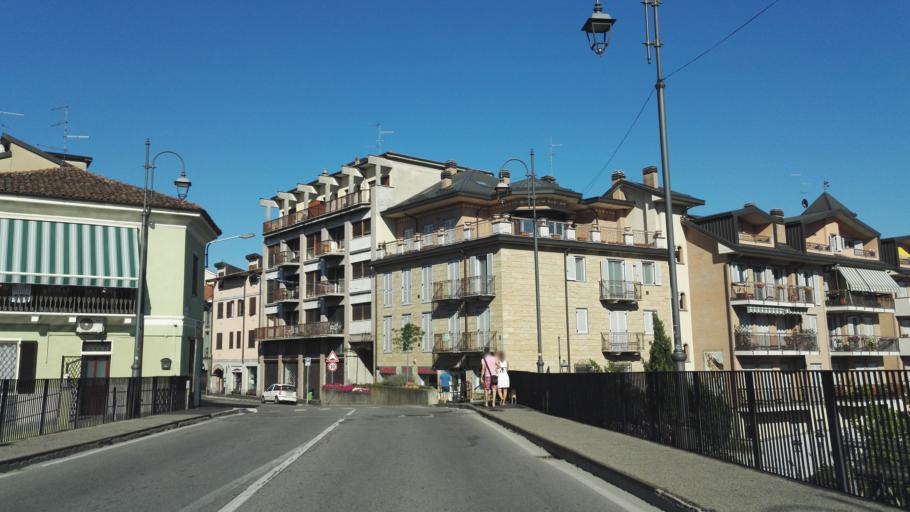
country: IT
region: Lombardy
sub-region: Citta metropolitana di Milano
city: Melegnano
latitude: 45.3575
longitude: 9.3262
